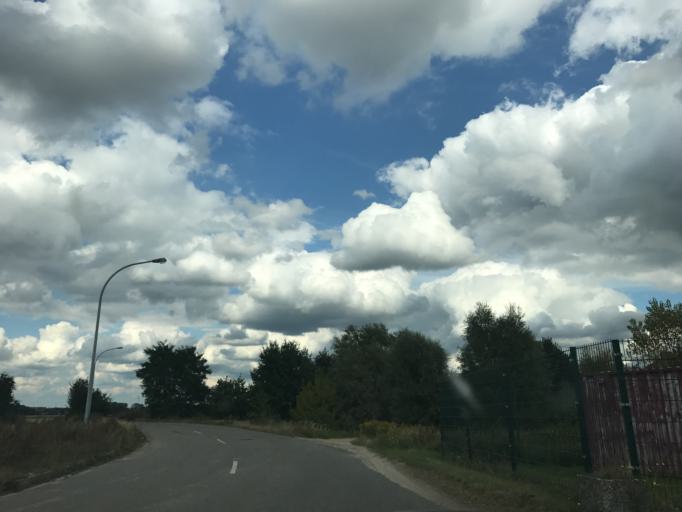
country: DE
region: Brandenburg
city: Wustermark
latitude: 52.4762
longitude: 12.9655
